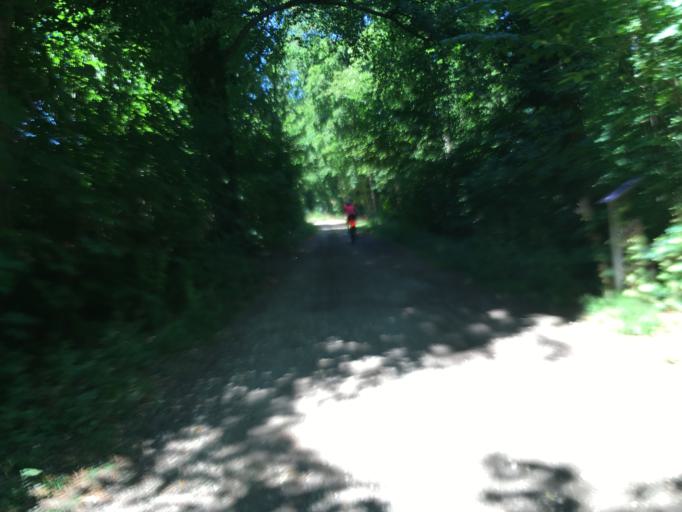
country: CH
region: Fribourg
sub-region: See District
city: Gurwolf
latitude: 46.9198
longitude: 7.0955
